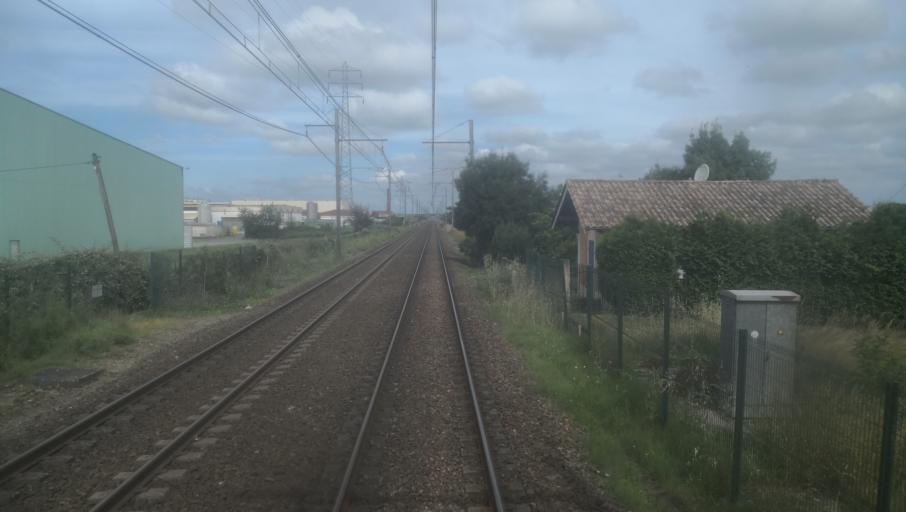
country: FR
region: Aquitaine
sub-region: Departement du Lot-et-Garonne
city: Marmande
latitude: 44.5104
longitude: 0.1518
